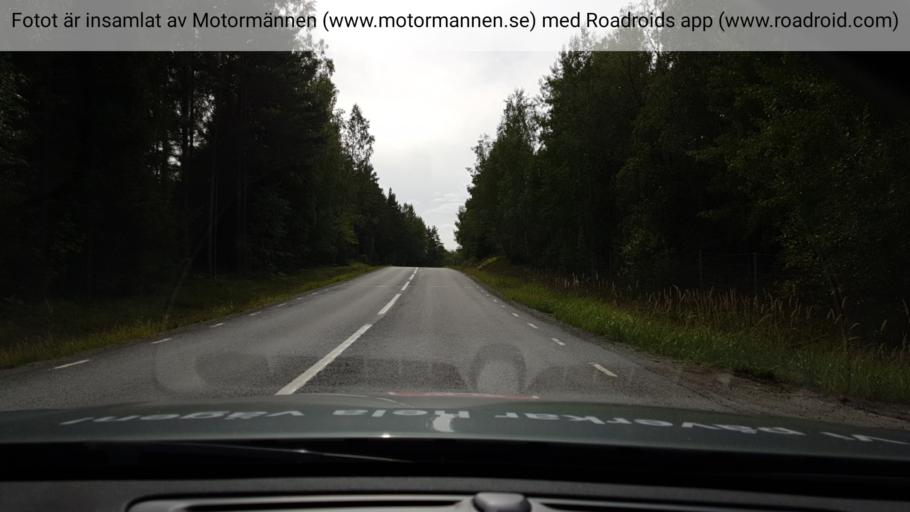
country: SE
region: Stockholm
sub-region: Botkyrka Kommun
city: Tullinge
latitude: 59.1245
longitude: 17.9049
